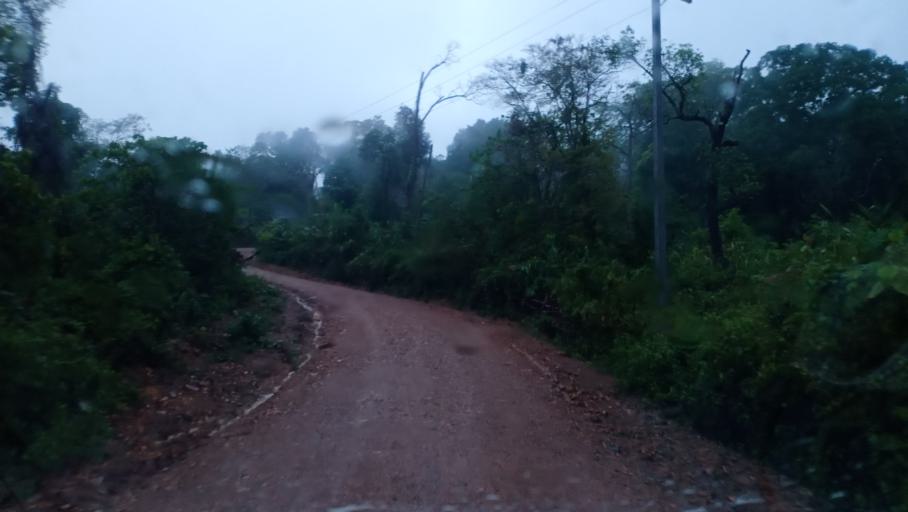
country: LA
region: Phongsali
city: Khoa
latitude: 21.1914
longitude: 102.2961
